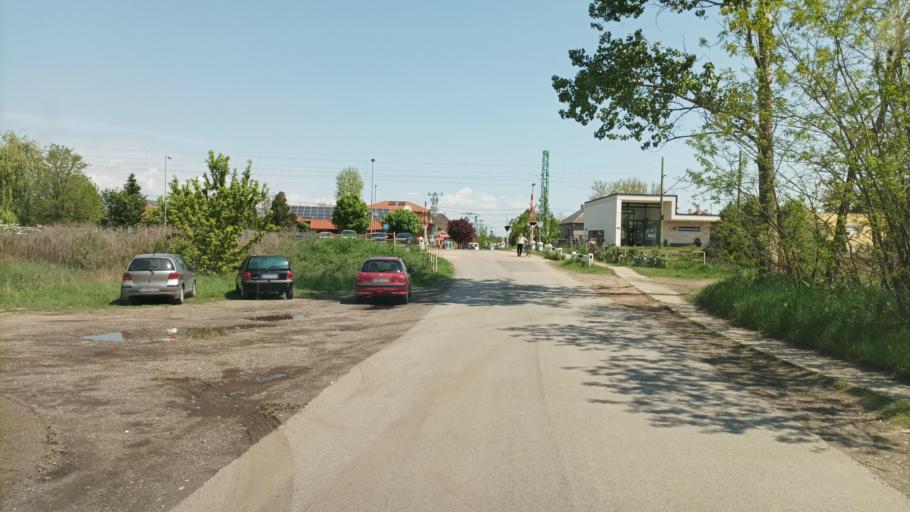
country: HU
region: Pest
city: Forropuszta
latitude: 47.4317
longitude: 19.6797
